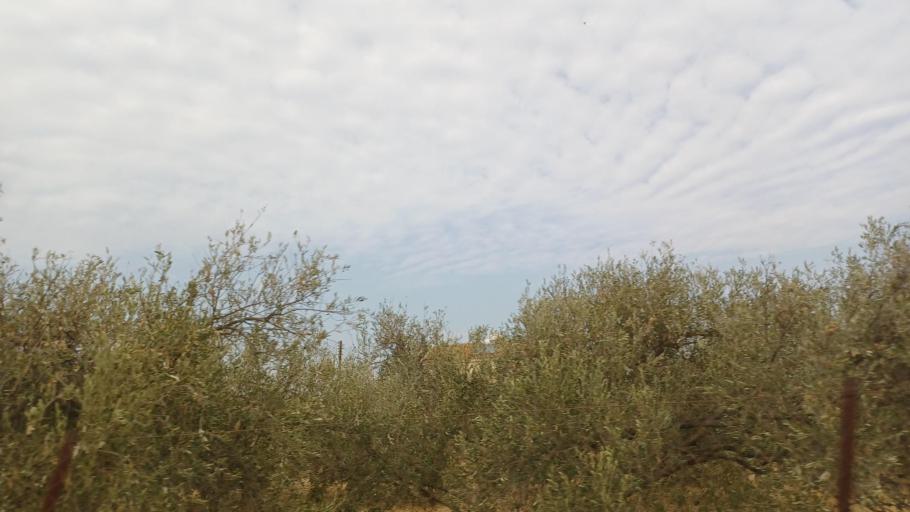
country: CY
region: Limassol
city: Ypsonas
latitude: 34.6816
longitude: 32.9547
